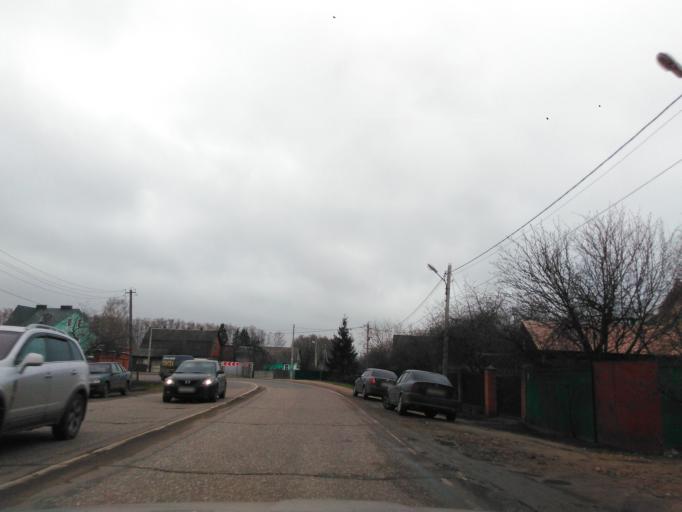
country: RU
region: Moskovskaya
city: Nakhabino
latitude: 55.8301
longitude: 37.1494
